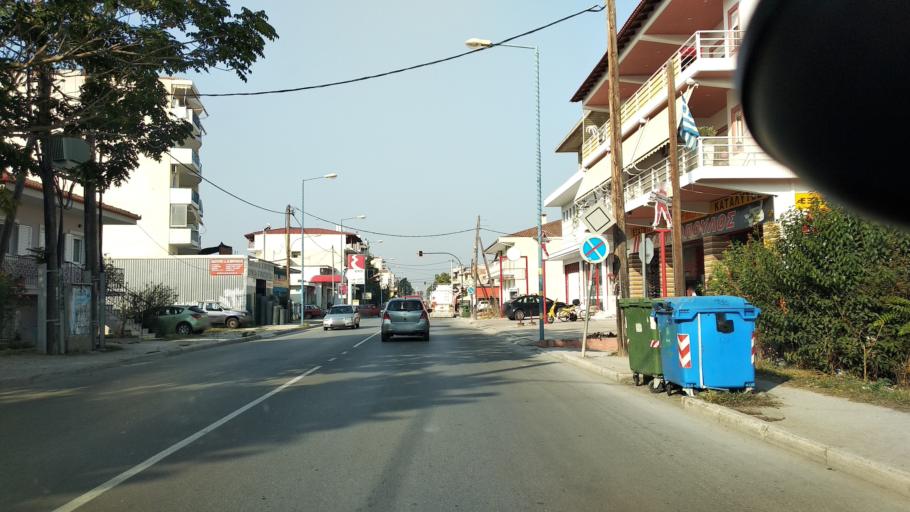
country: GR
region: Thessaly
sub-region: Nomos Larisis
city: Larisa
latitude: 39.6329
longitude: 22.3918
